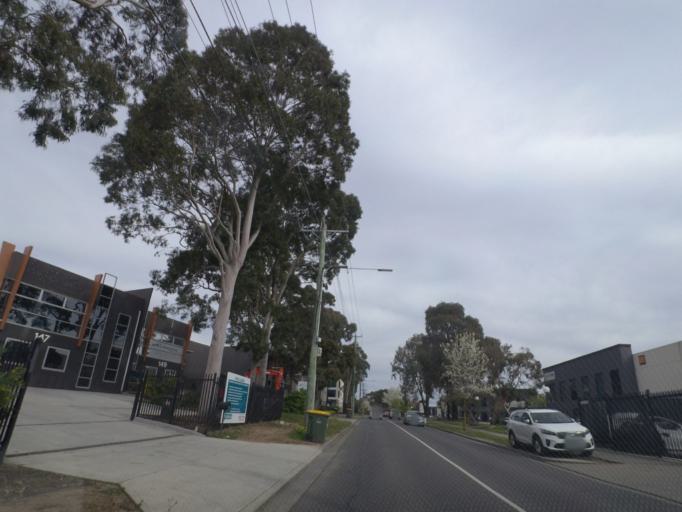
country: AU
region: Victoria
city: Forest Hill
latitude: -37.8315
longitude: 145.1873
